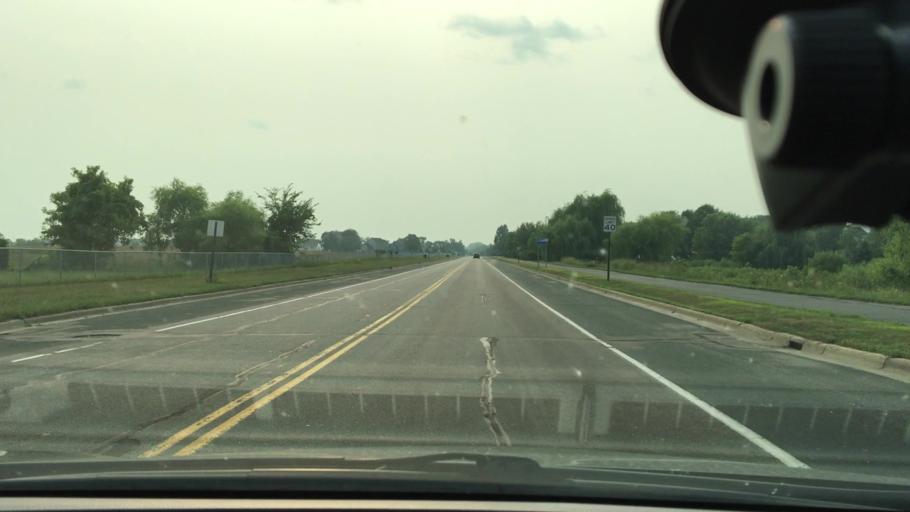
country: US
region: Minnesota
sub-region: Wright County
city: Otsego
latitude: 45.2633
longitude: -93.5612
